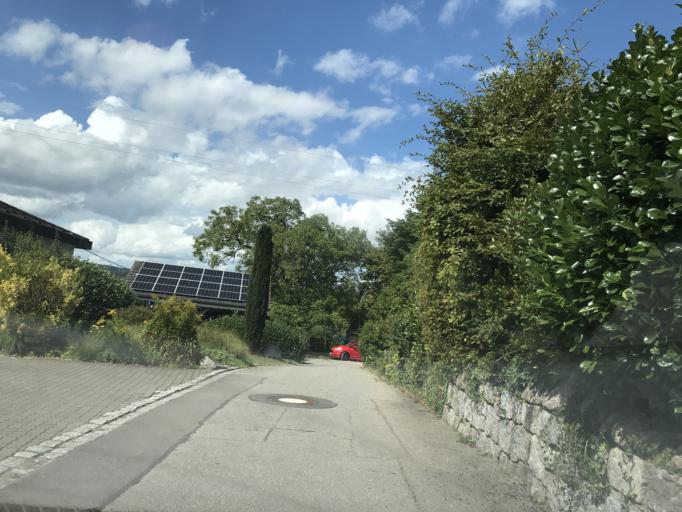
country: DE
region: Baden-Wuerttemberg
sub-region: Freiburg Region
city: Steinen
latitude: 47.6003
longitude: 7.7533
